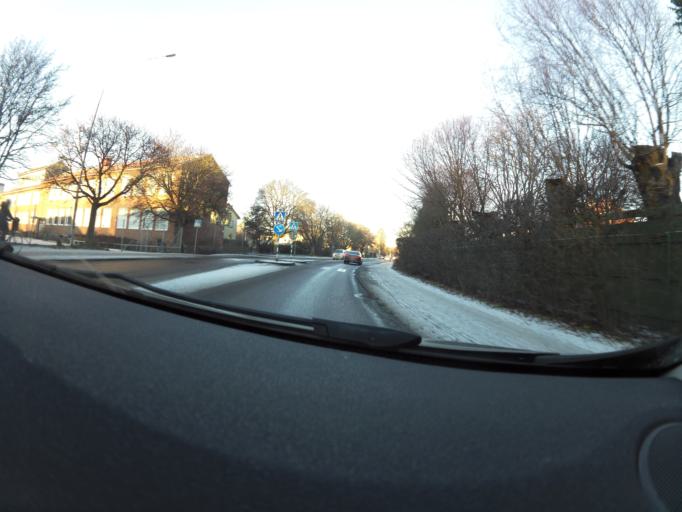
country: SE
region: Gaevleborg
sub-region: Gavle Kommun
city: Gavle
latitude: 60.6683
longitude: 17.1342
